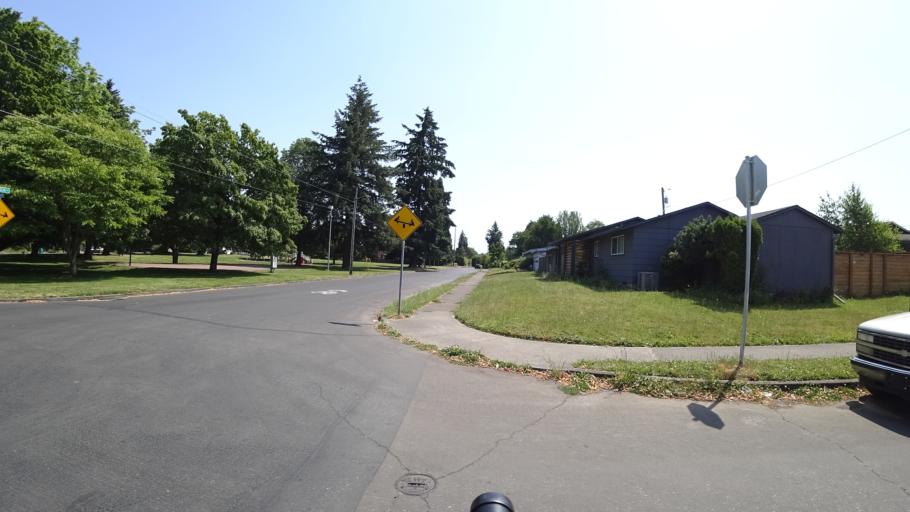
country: US
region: Washington
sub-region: Clark County
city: Vancouver
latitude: 45.5886
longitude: -122.7025
